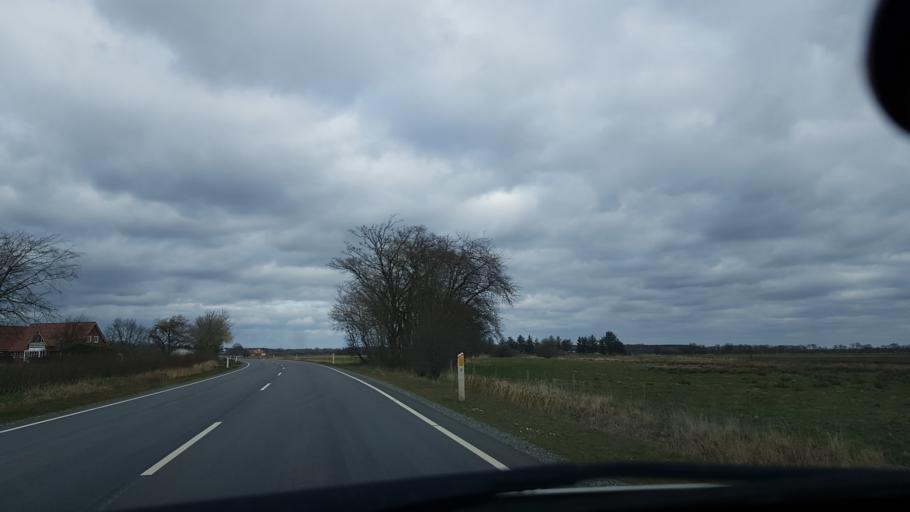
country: DK
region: South Denmark
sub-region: Vejen Kommune
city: Holsted
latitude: 55.4178
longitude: 8.8927
